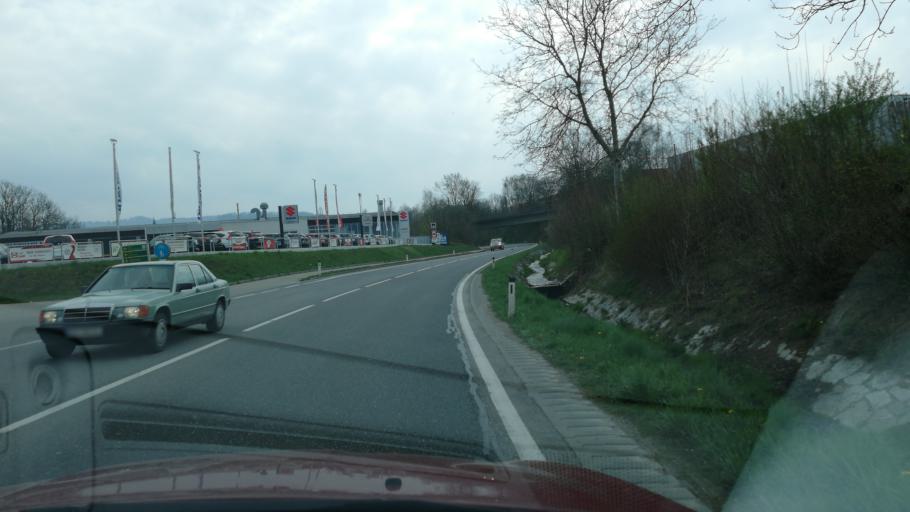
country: AT
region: Upper Austria
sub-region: Politischer Bezirk Vocklabruck
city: Lenzing
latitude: 47.9563
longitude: 13.6068
